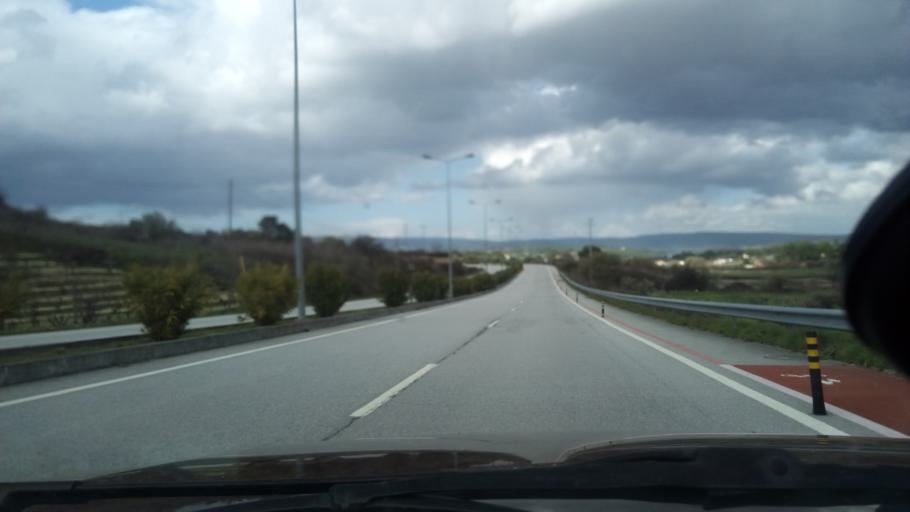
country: PT
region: Guarda
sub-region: Celorico da Beira
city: Celorico da Beira
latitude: 40.6345
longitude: -7.3853
